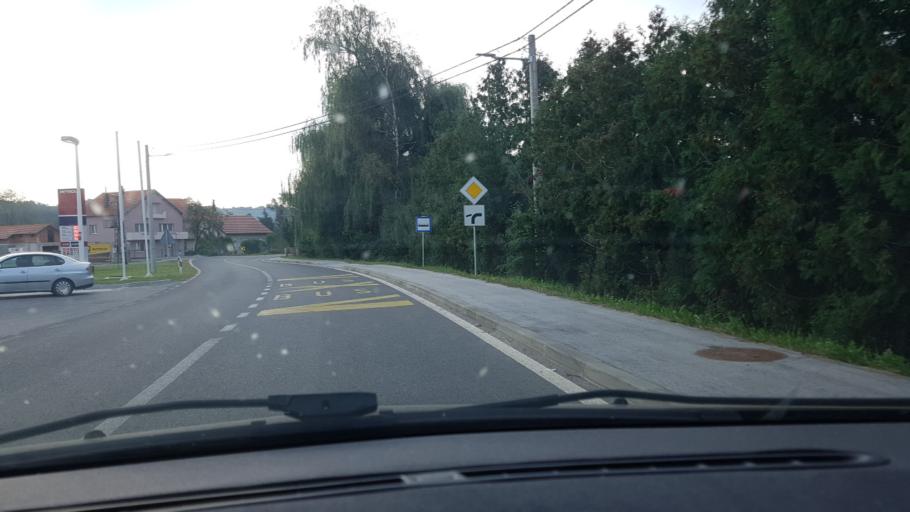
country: HR
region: Krapinsko-Zagorska
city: Zlatar
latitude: 46.1027
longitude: 16.0614
